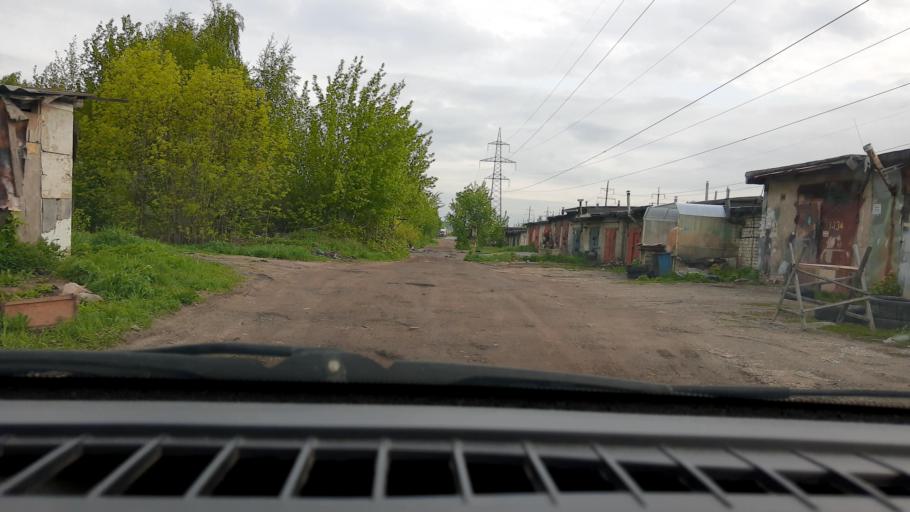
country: RU
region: Nizjnij Novgorod
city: Nizhniy Novgorod
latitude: 56.2727
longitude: 43.8975
